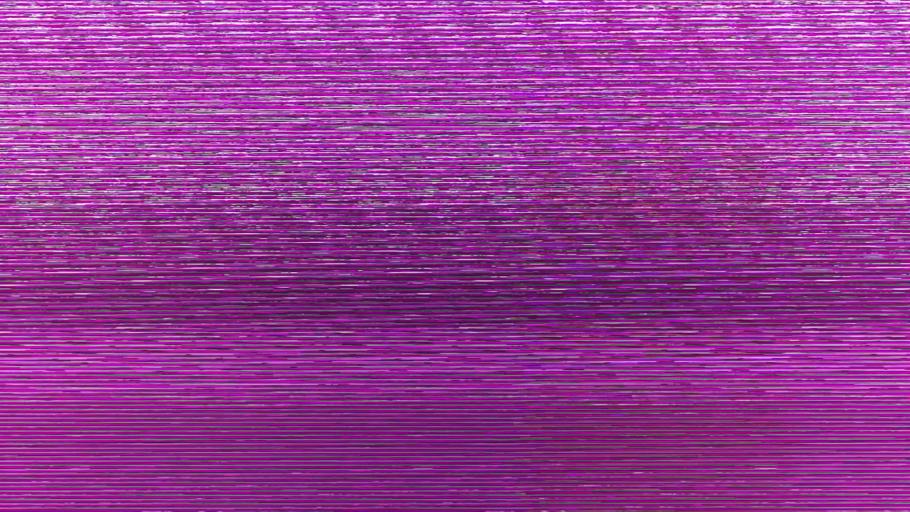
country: US
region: Michigan
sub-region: Genesee County
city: Linden
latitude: 42.8203
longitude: -83.7825
